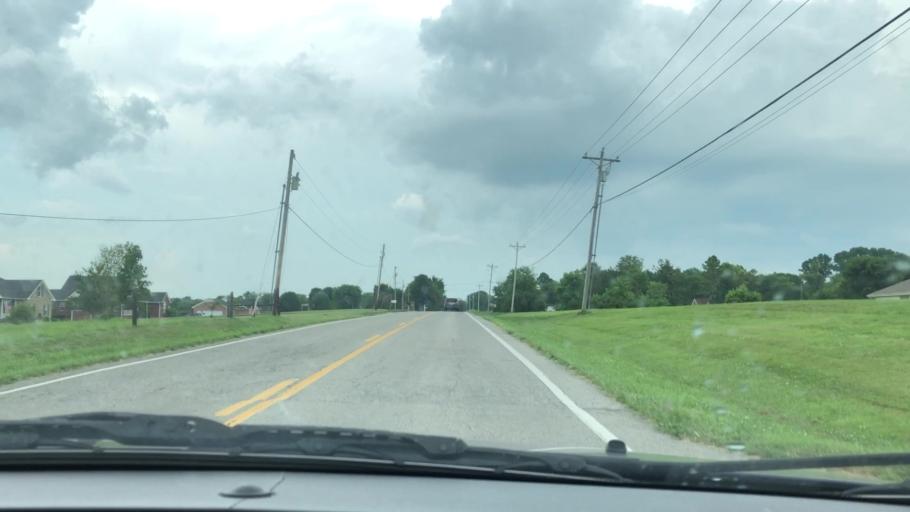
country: US
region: Tennessee
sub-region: Maury County
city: Spring Hill
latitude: 35.7337
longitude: -87.0107
